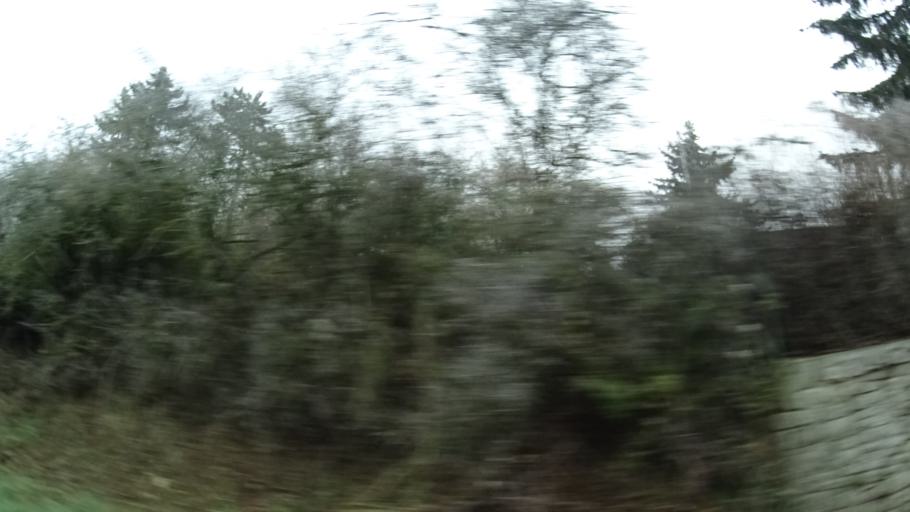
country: DE
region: Bavaria
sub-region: Regierungsbezirk Unterfranken
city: Sulzfeld am Main
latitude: 49.7197
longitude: 10.1473
